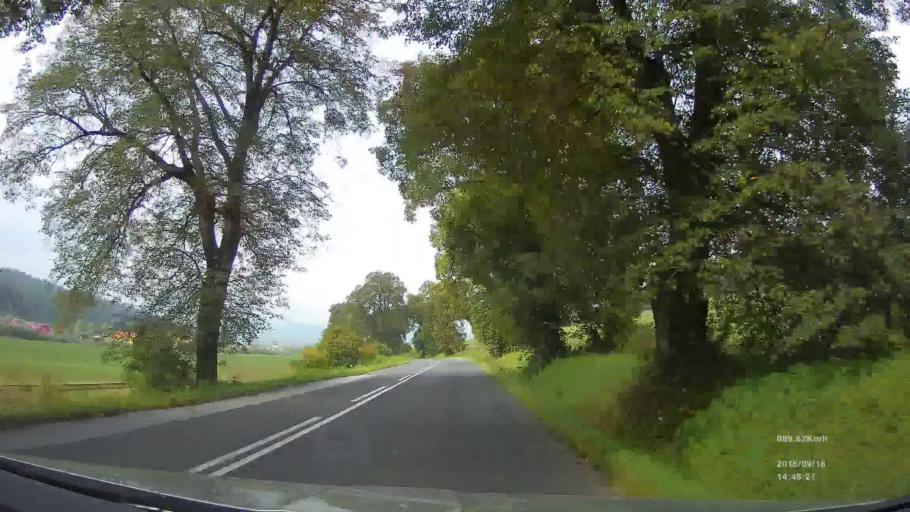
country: SK
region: Kosicky
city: Spisska Nova Ves
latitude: 48.9763
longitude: 20.5819
